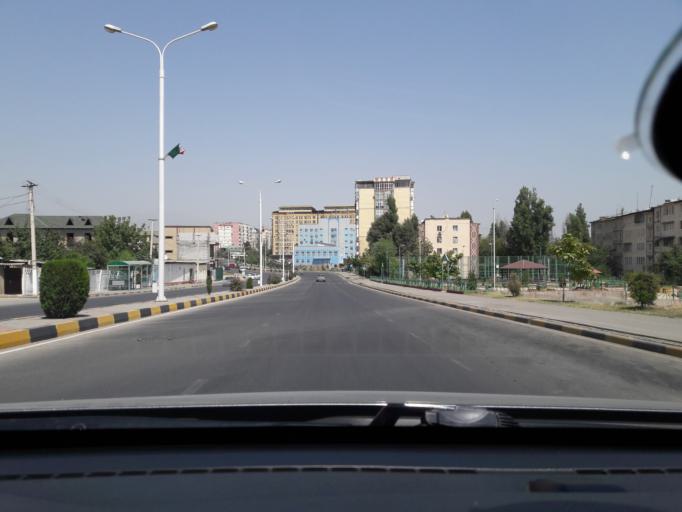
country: TJ
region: Dushanbe
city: Dushanbe
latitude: 38.5850
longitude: 68.7103
